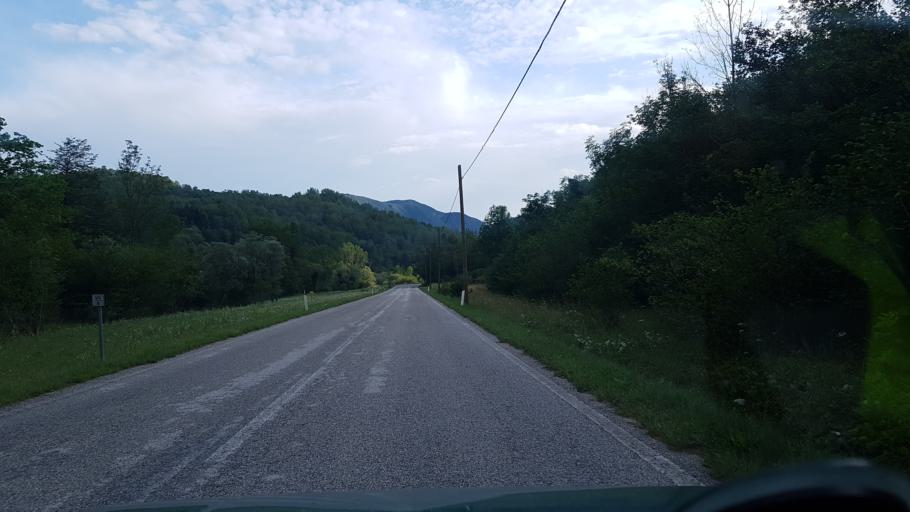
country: IT
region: Friuli Venezia Giulia
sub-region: Provincia di Udine
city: Lusevera
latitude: 46.2870
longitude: 13.2673
